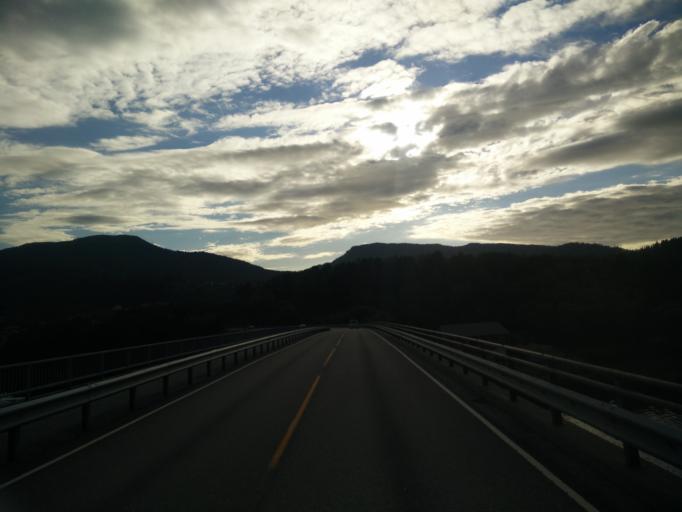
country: NO
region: More og Romsdal
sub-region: Kristiansund
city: Rensvik
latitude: 63.0125
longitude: 7.9863
